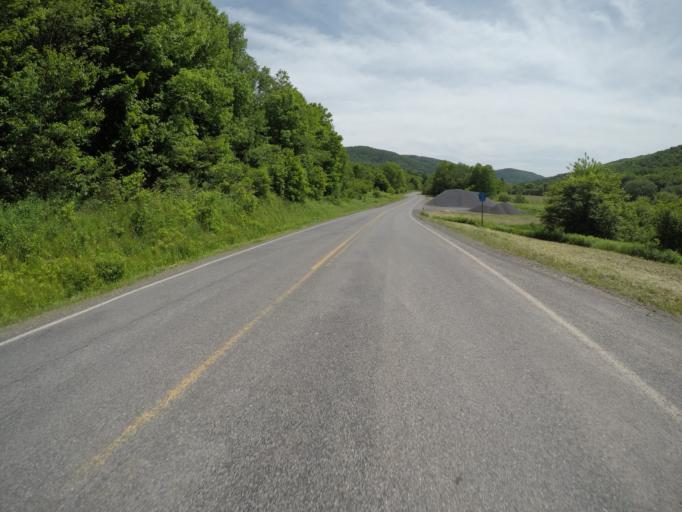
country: US
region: New York
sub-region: Delaware County
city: Delhi
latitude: 42.1558
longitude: -74.7980
